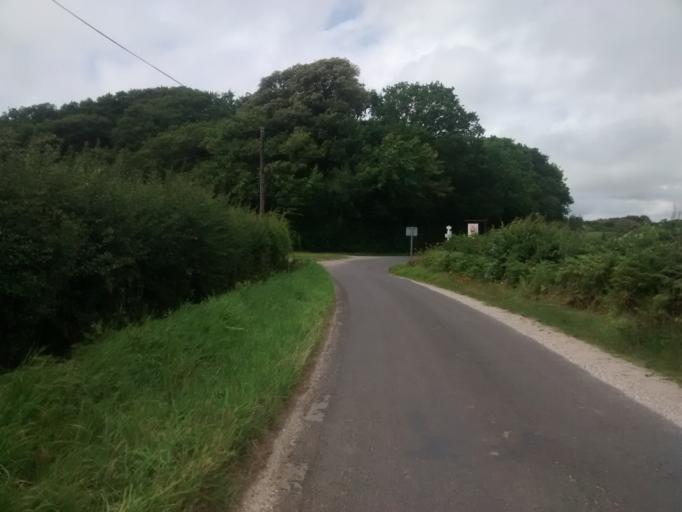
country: GB
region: England
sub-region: Dorset
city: Wareham
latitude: 50.6423
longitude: -2.0966
